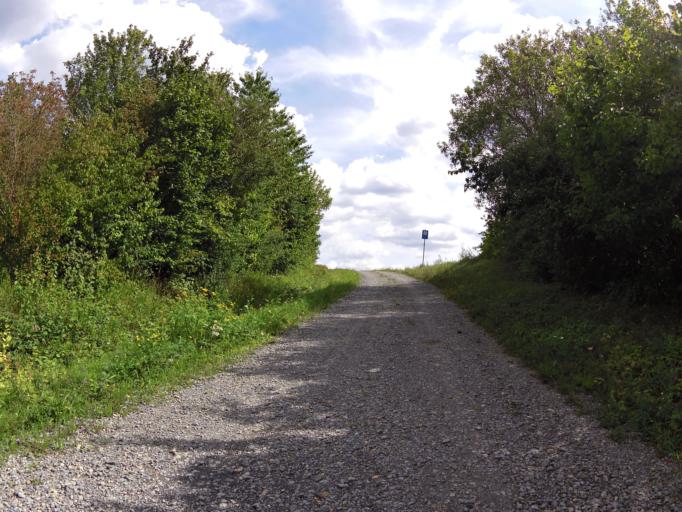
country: DE
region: Bavaria
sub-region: Regierungsbezirk Unterfranken
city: Margetshochheim
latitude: 49.8361
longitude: 9.8425
